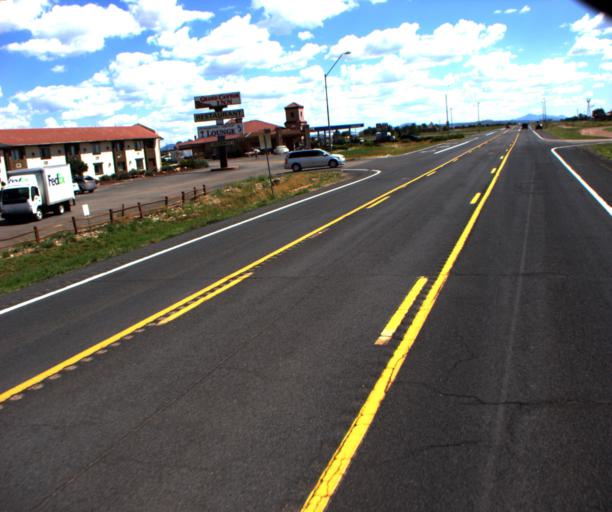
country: US
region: Arizona
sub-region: Coconino County
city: Grand Canyon Village
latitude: 35.6543
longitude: -112.1392
